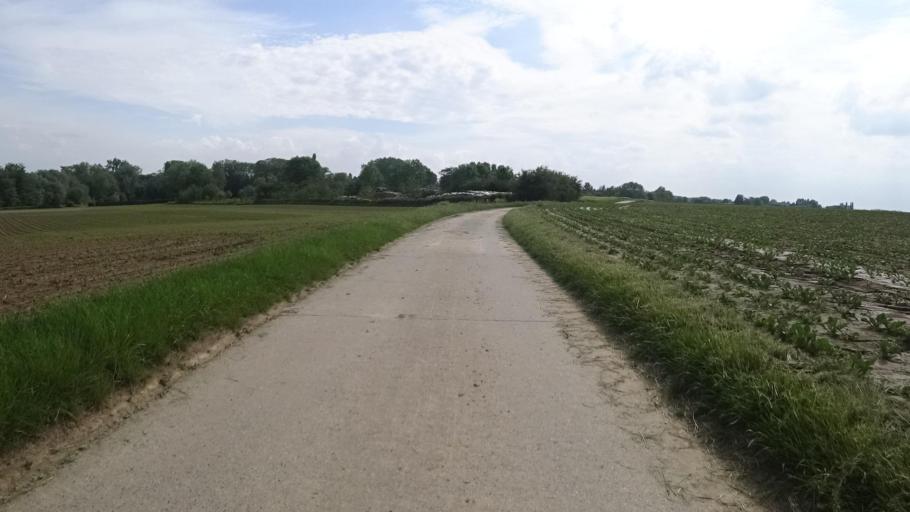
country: BE
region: Wallonia
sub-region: Province du Brabant Wallon
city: Walhain-Saint-Paul
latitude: 50.6420
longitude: 4.6659
